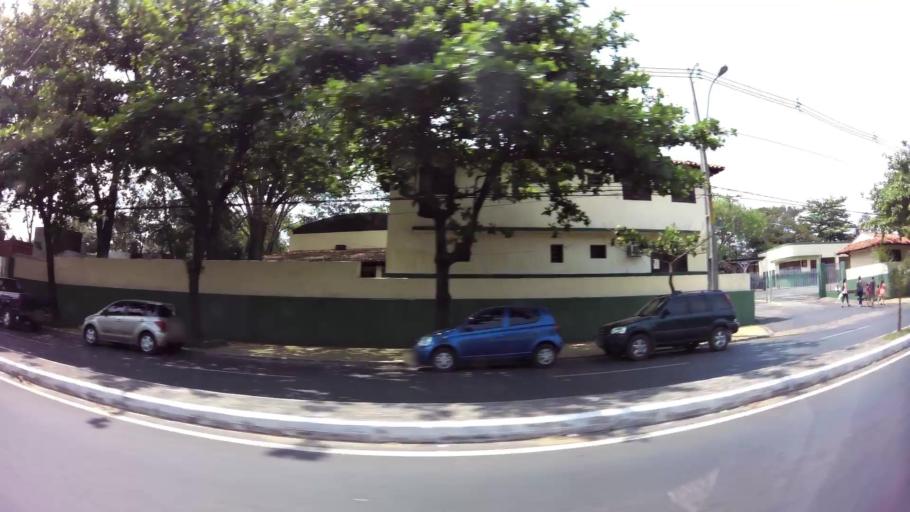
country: PY
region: Asuncion
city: Asuncion
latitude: -25.2935
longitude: -57.5920
